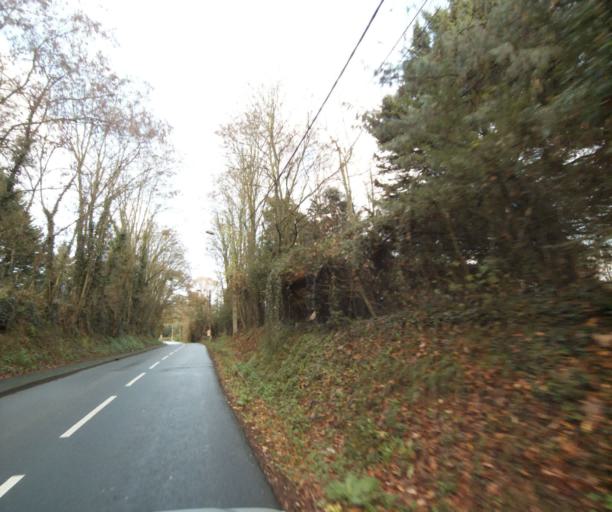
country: FR
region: Pays de la Loire
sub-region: Departement de la Sarthe
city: Sarge-les-le-Mans
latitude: 48.0080
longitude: 0.2341
